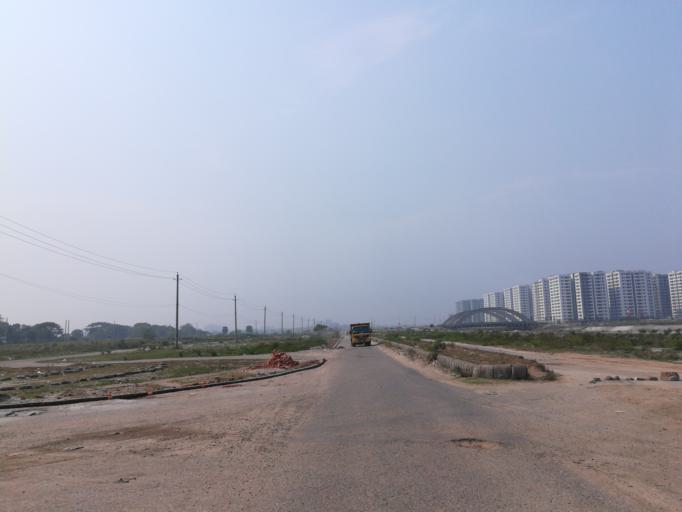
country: BD
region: Dhaka
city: Tungi
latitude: 23.8617
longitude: 90.3600
